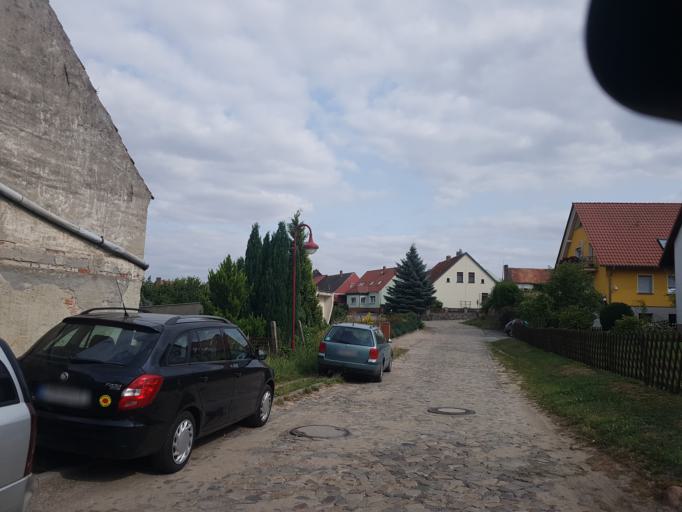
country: DE
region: Brandenburg
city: Gorzke
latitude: 52.1122
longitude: 12.3727
